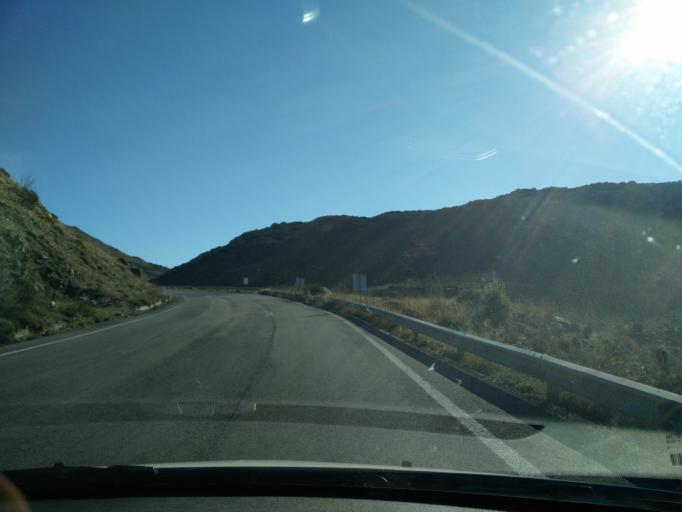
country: GR
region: Crete
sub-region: Nomos Irakleiou
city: Arkalochori
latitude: 35.0671
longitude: 25.3545
